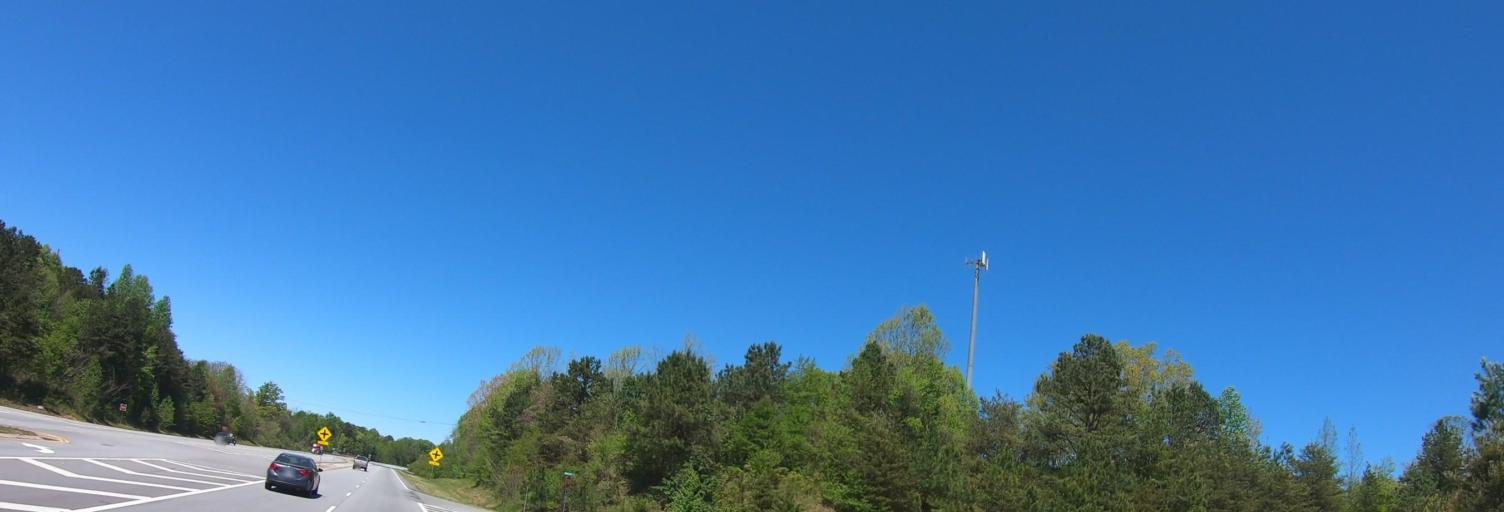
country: US
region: Georgia
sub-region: Habersham County
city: Clarkesville
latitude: 34.6842
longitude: -83.4243
